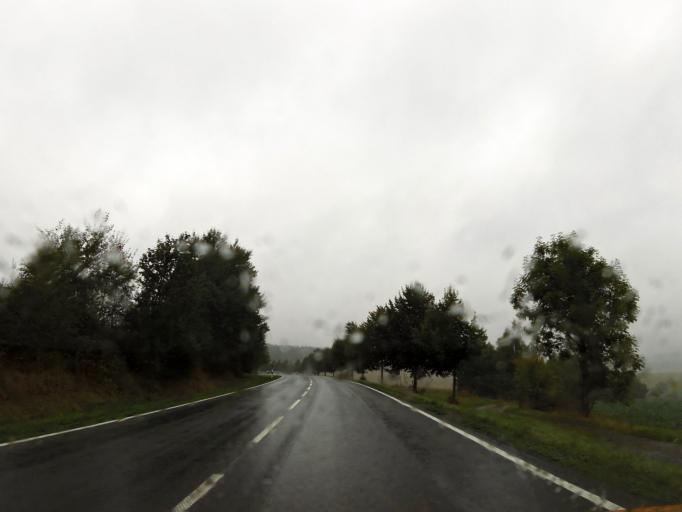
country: DE
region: Saxony-Anhalt
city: Friedrichsbrunn
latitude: 51.6496
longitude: 11.0261
